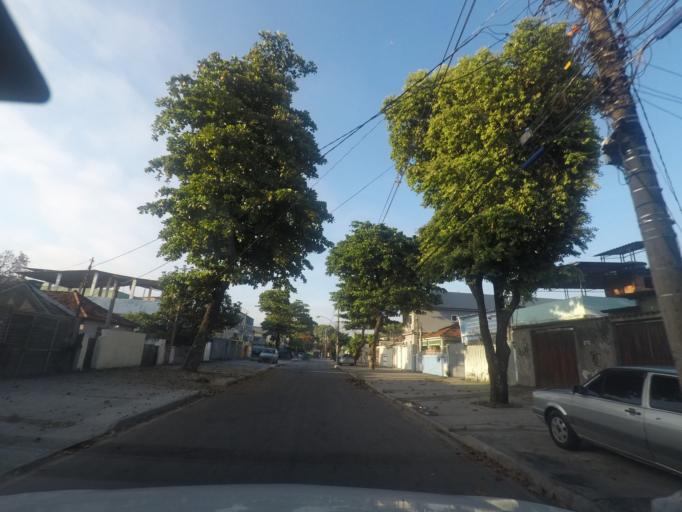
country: BR
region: Rio de Janeiro
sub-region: Duque De Caxias
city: Duque de Caxias
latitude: -22.8310
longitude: -43.2710
